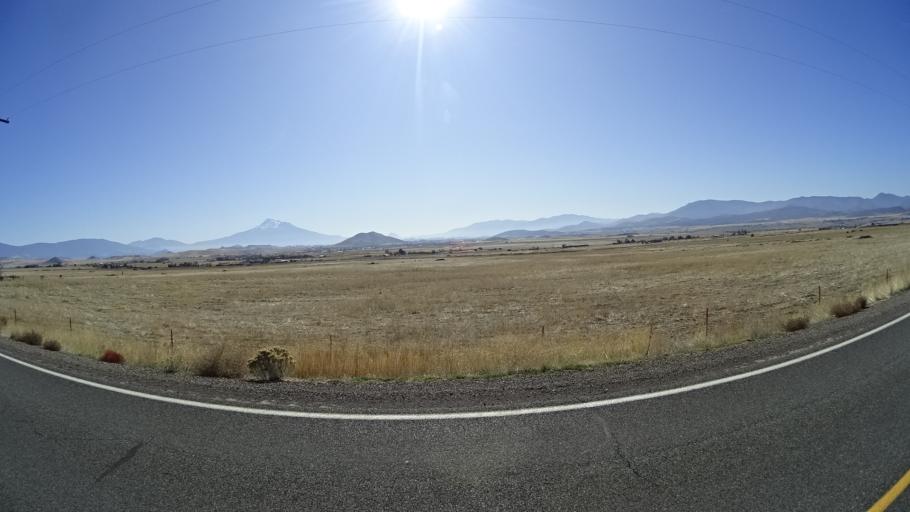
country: US
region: California
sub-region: Siskiyou County
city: Montague
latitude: 41.7698
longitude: -122.5463
